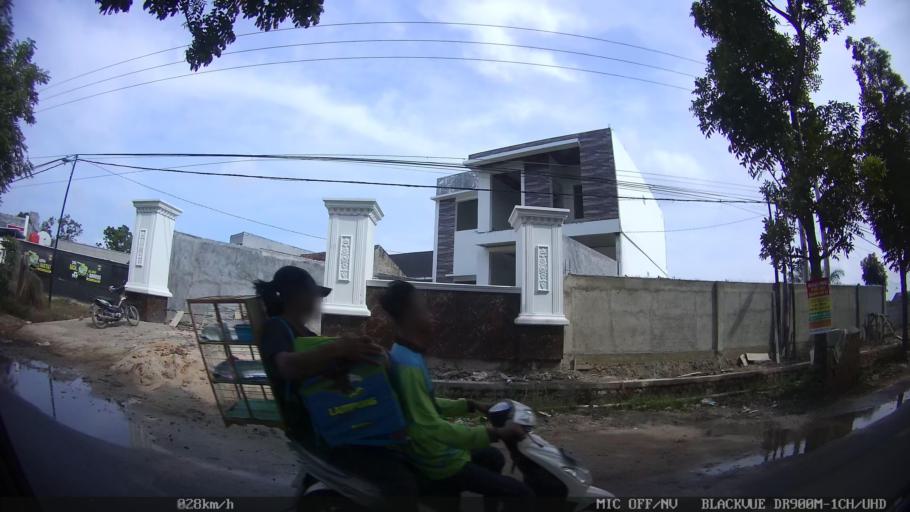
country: ID
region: Lampung
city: Kedaton
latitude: -5.3766
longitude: 105.3058
